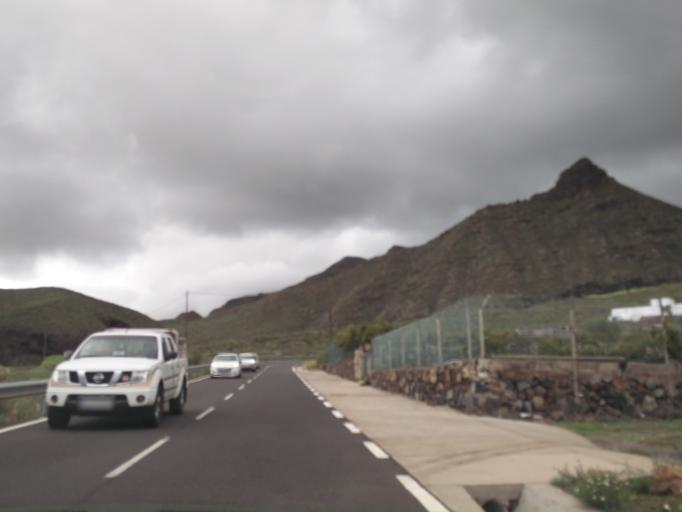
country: ES
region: Canary Islands
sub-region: Provincia de Santa Cruz de Tenerife
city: Arona
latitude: 28.1093
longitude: -16.6850
